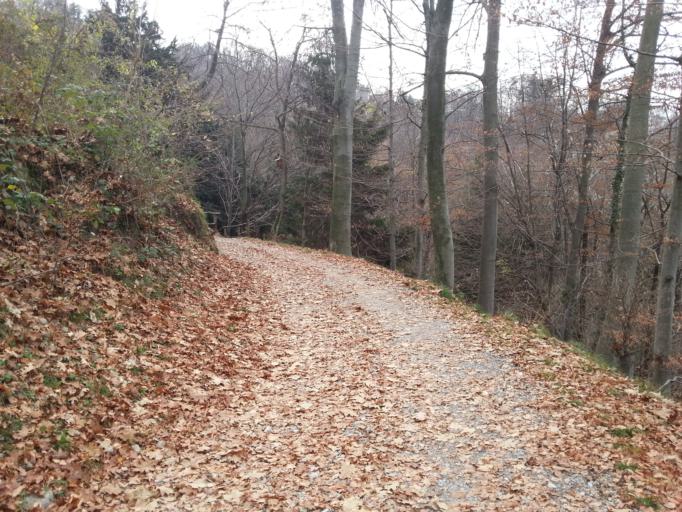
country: CH
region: Ticino
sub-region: Mendrisio District
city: Morbio Inferiore
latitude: 45.8659
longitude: 9.0266
